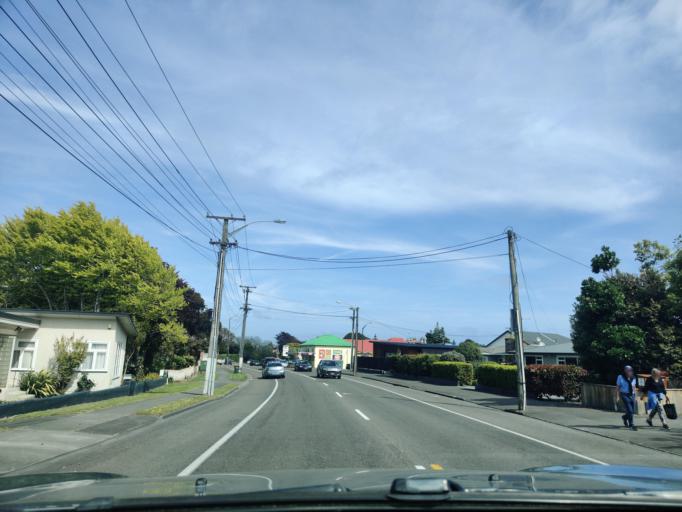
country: NZ
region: Manawatu-Wanganui
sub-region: Wanganui District
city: Wanganui
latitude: -39.9177
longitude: 175.0381
